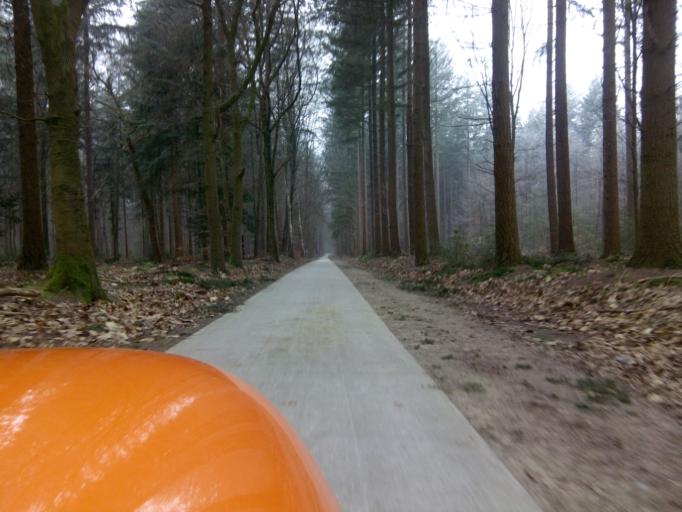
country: NL
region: Gelderland
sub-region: Gemeente Putten
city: Putten
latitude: 52.2517
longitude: 5.6389
